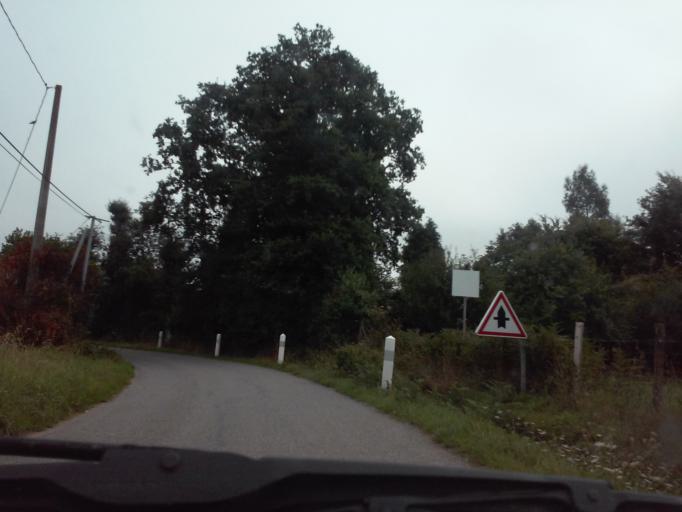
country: FR
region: Brittany
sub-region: Departement du Morbihan
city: Taupont
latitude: 48.0080
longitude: -2.4571
